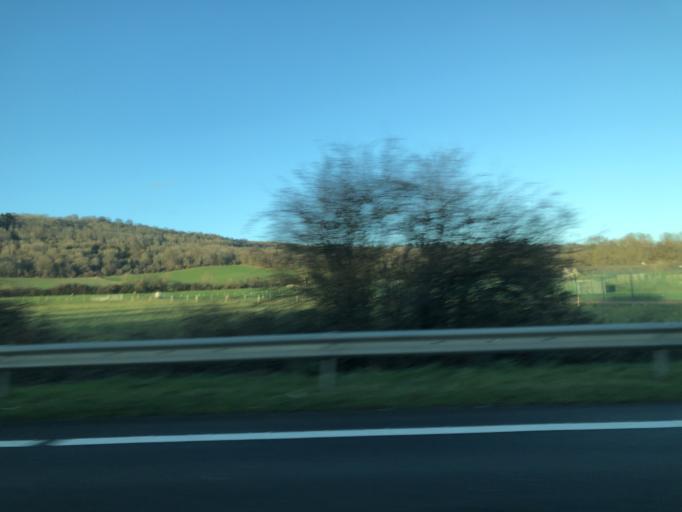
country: GB
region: England
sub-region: Surrey
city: Oxted
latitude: 51.2685
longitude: 0.0030
